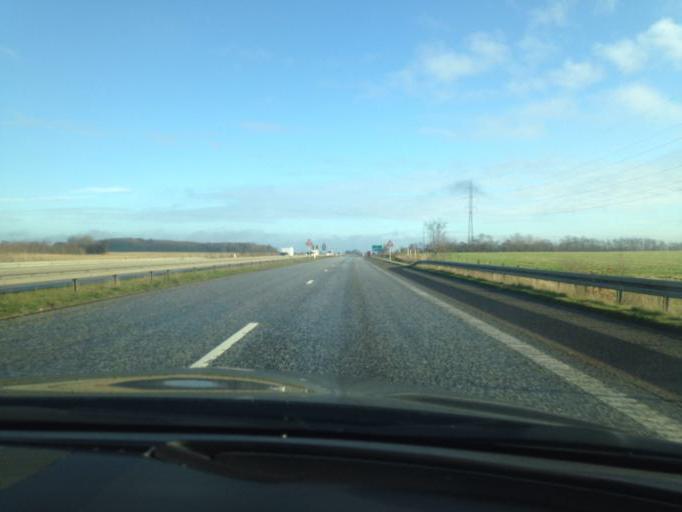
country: DK
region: South Denmark
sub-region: Kolding Kommune
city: Lunderskov
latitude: 55.5064
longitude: 9.2955
